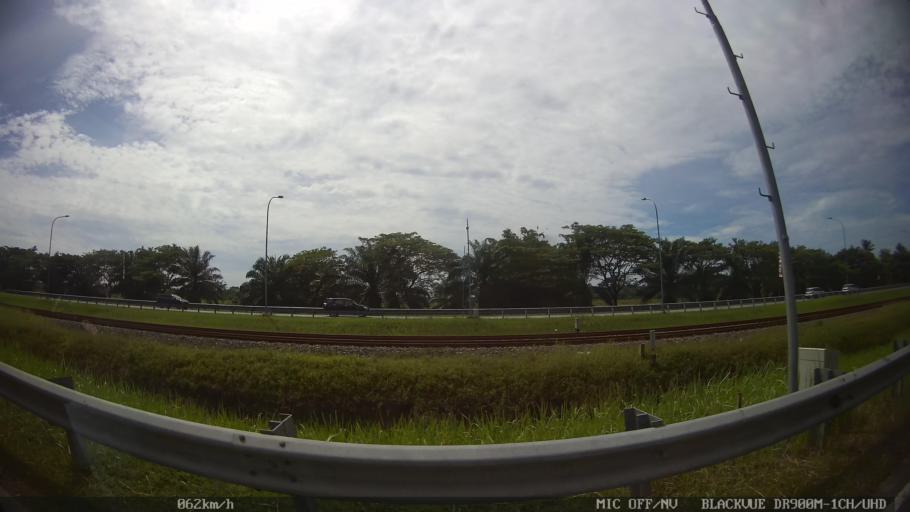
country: ID
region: North Sumatra
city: Percut
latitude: 3.6280
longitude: 98.8713
